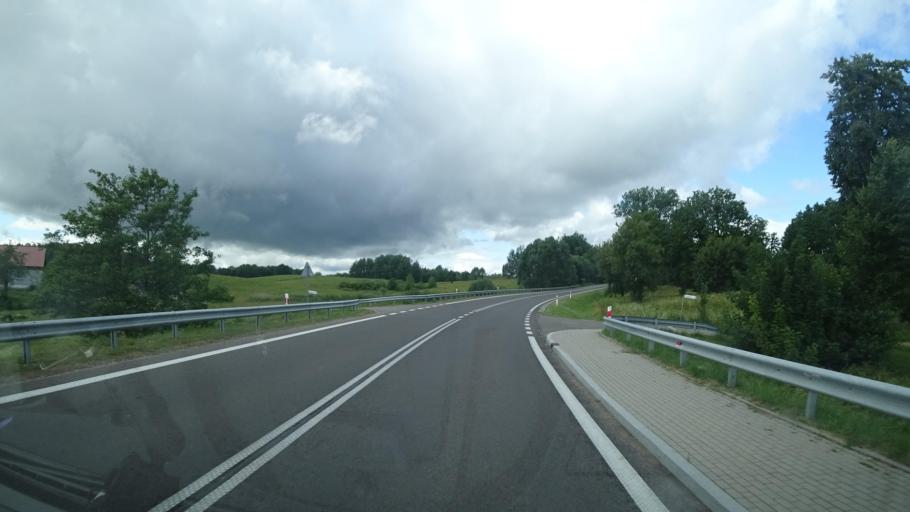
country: PL
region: Warmian-Masurian Voivodeship
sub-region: Powiat olecki
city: Kowale Oleckie
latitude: 54.2521
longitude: 22.3826
